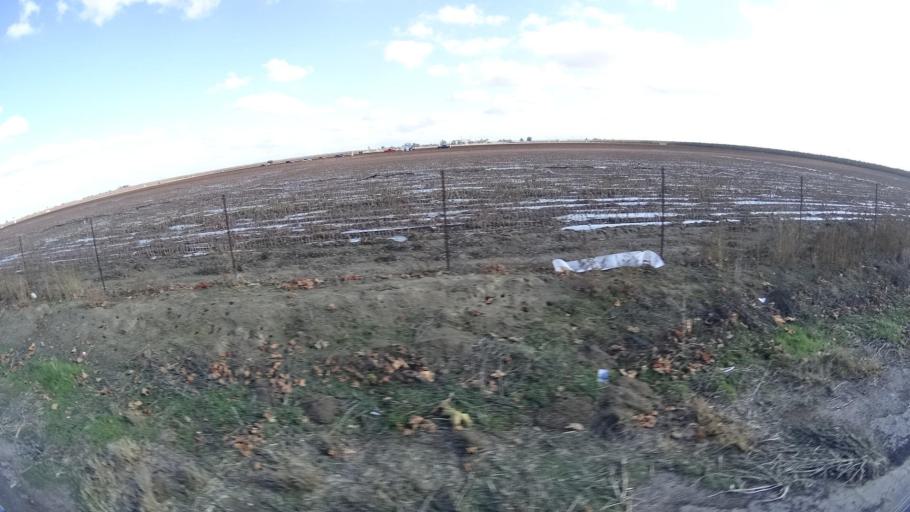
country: US
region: California
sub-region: Kern County
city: Delano
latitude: 35.7201
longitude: -119.2586
